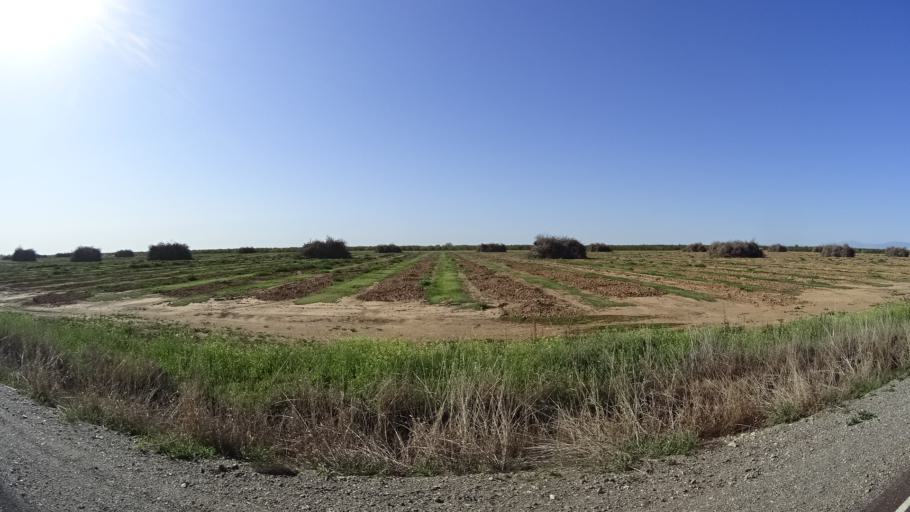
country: US
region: California
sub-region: Glenn County
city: Hamilton City
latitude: 39.7666
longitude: -122.0738
